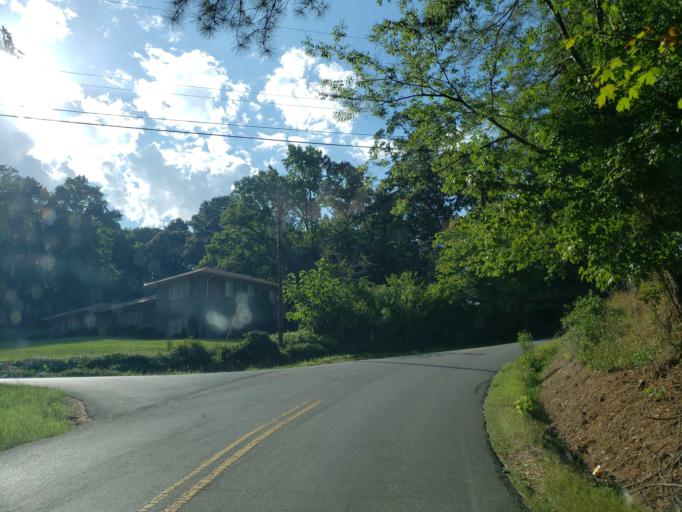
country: US
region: Georgia
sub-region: Floyd County
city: Rome
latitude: 34.2314
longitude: -85.1444
